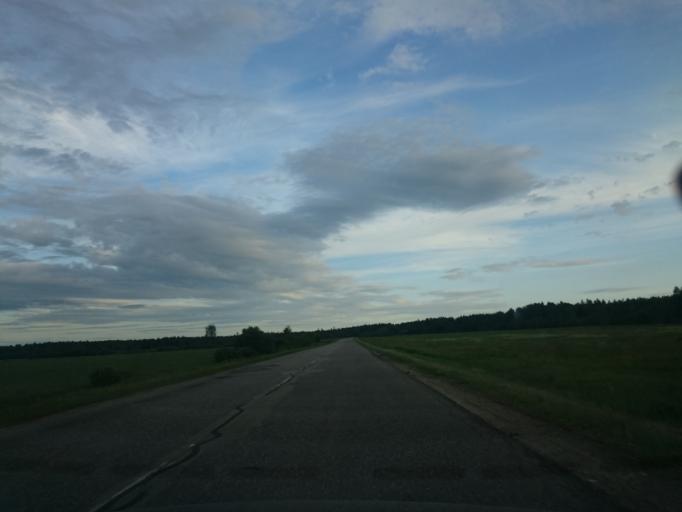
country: LV
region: Incukalns
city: Incukalns
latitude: 57.0752
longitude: 24.6689
